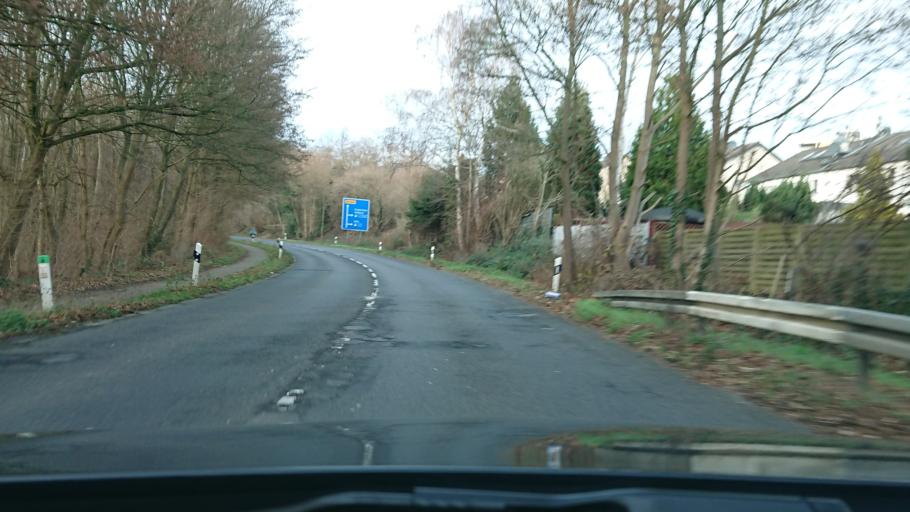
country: DE
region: North Rhine-Westphalia
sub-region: Regierungsbezirk Koln
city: Frechen
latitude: 50.8855
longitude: 6.8221
